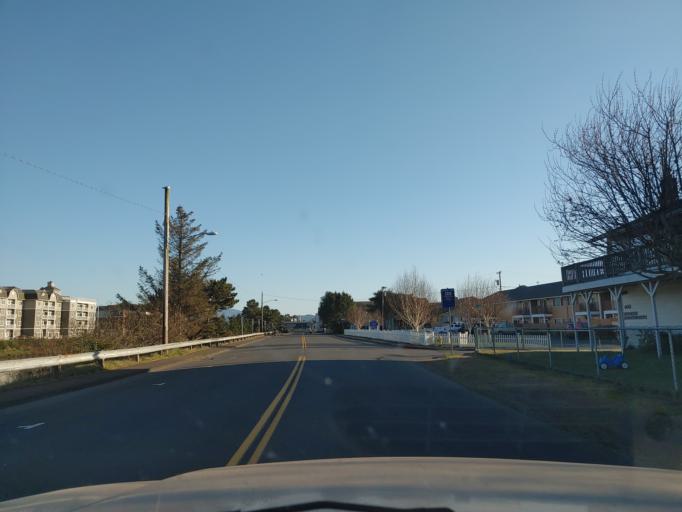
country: US
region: Oregon
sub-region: Clatsop County
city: Seaside
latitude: 45.9966
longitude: -123.9245
